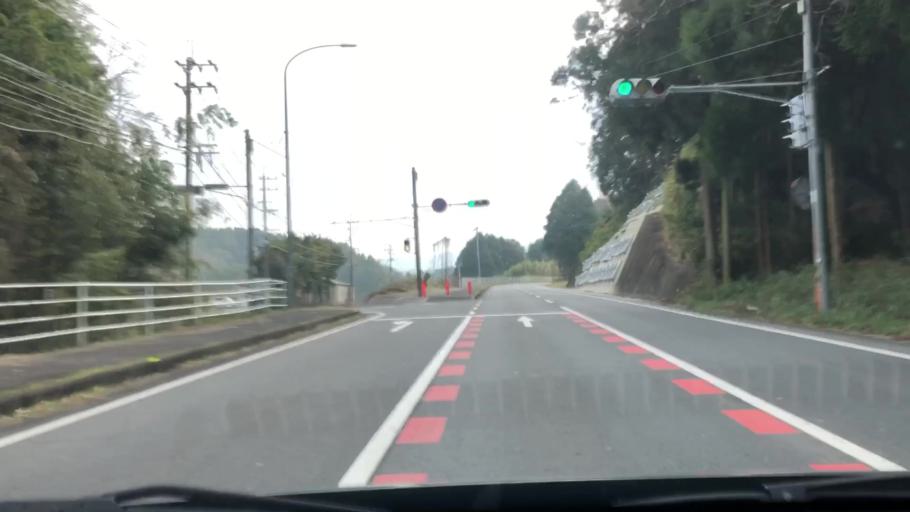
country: JP
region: Oita
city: Takedamachi
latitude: 32.9787
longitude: 131.5565
